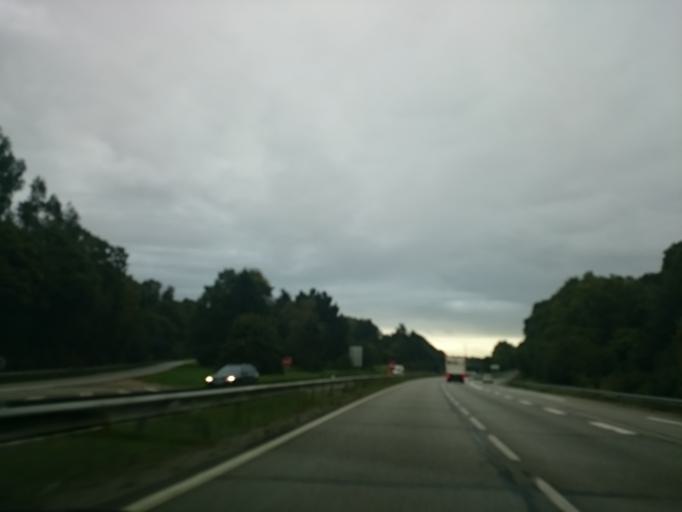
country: FR
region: Brittany
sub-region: Departement du Finistere
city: Quimper
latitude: 48.0230
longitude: -4.0841
